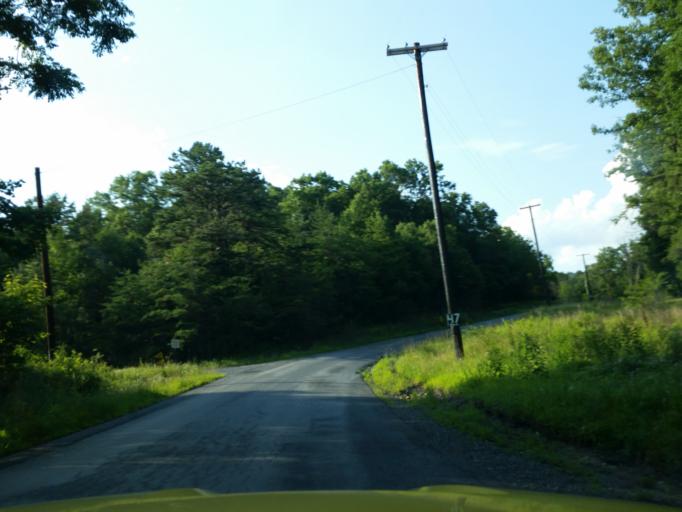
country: US
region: Pennsylvania
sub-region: Dauphin County
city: Williamstown
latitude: 40.4524
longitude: -76.6271
